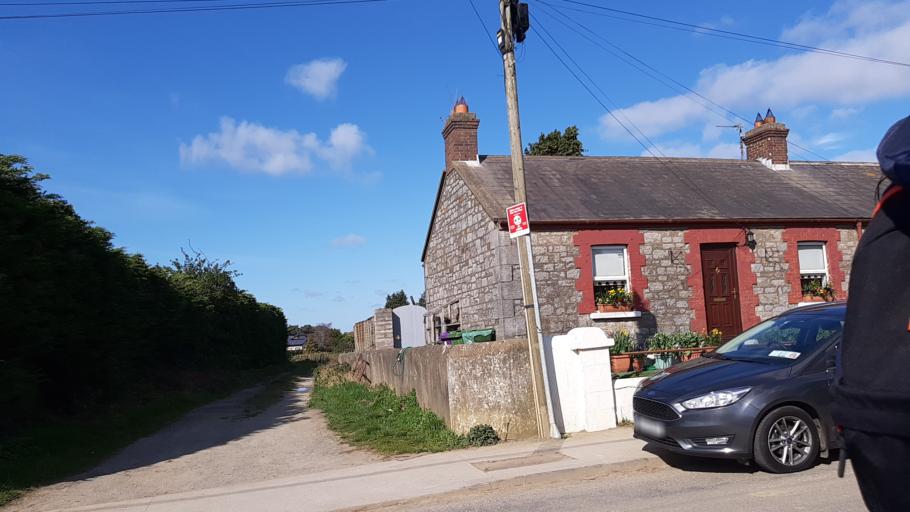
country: IE
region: Leinster
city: Malahide
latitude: 53.4348
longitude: -6.1669
